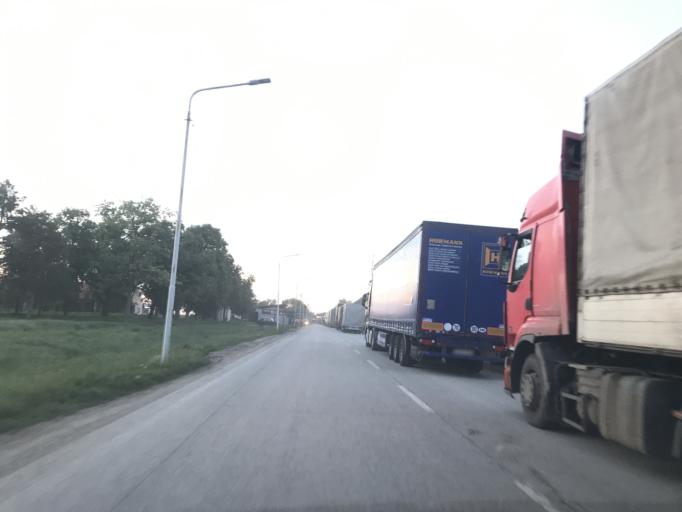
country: RS
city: Srpska Crnja
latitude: 45.7459
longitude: 20.6997
